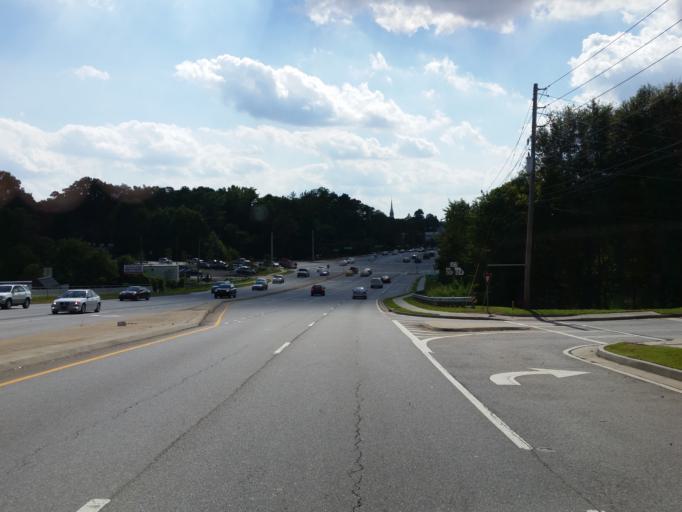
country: US
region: Georgia
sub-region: Gwinnett County
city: Lawrenceville
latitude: 33.9572
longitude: -83.9772
